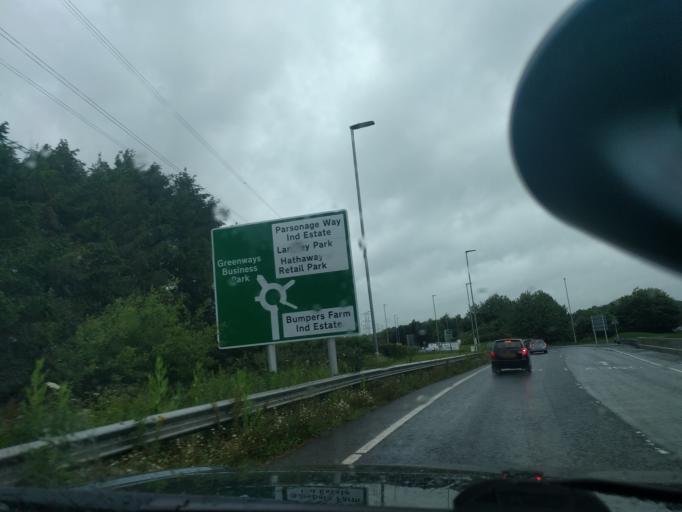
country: GB
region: England
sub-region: Wiltshire
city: Chippenham
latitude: 51.4680
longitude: -2.1448
